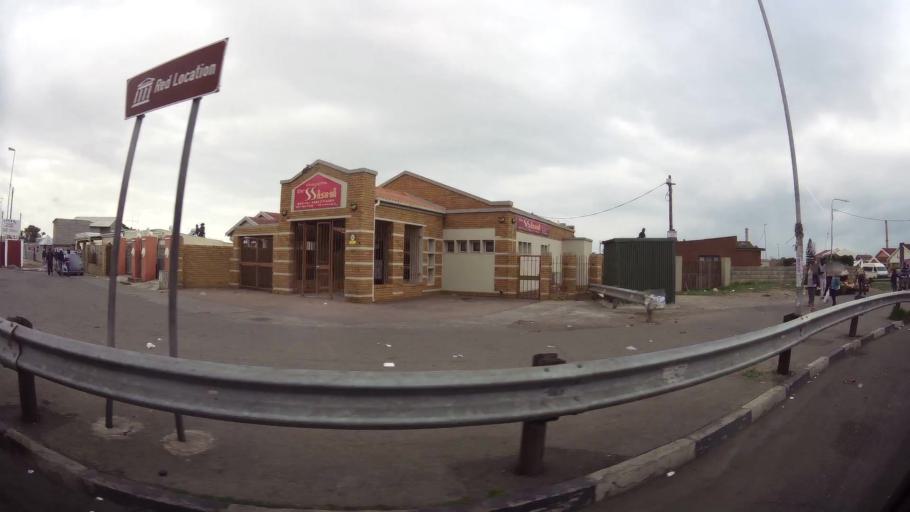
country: ZA
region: Eastern Cape
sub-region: Nelson Mandela Bay Metropolitan Municipality
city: Port Elizabeth
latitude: -33.9066
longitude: 25.5980
